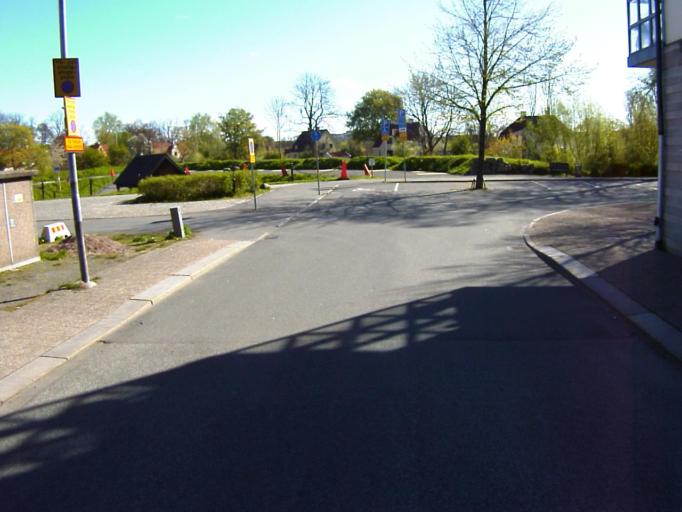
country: SE
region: Skane
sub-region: Kristianstads Kommun
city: Kristianstad
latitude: 56.0341
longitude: 14.1547
